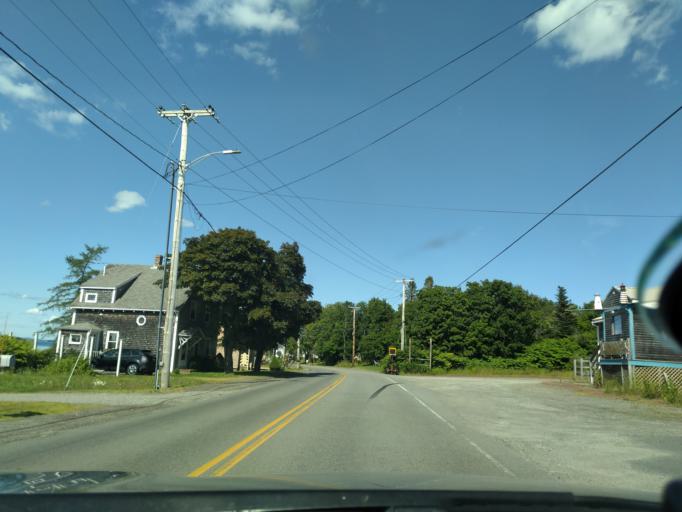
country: US
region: Maine
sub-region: Washington County
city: Eastport
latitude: 44.8525
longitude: -66.9954
